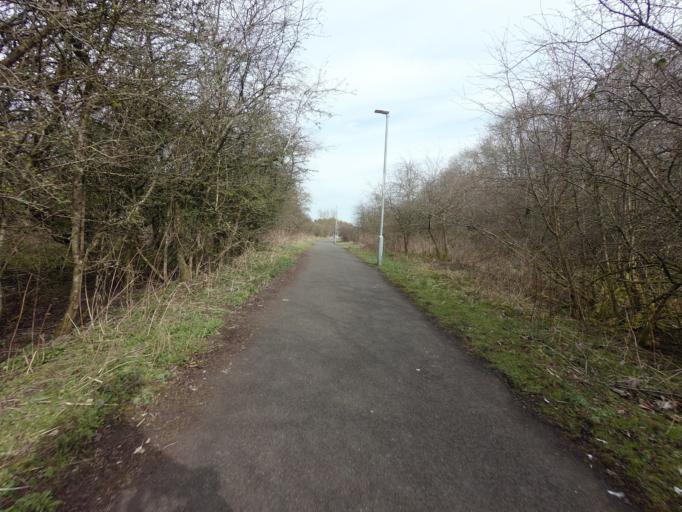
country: GB
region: Scotland
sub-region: West Lothian
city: Livingston
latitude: 55.9250
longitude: -3.5026
